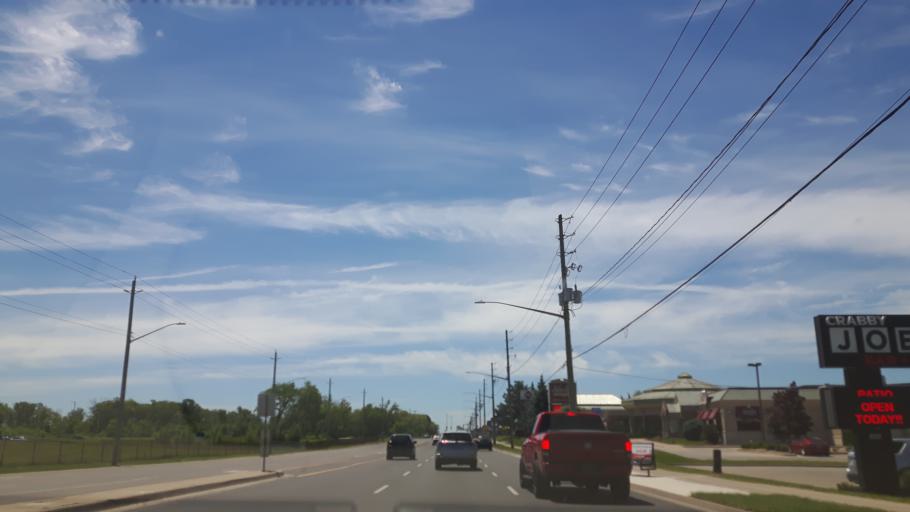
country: CA
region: Ontario
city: London
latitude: 42.9546
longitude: -81.2295
